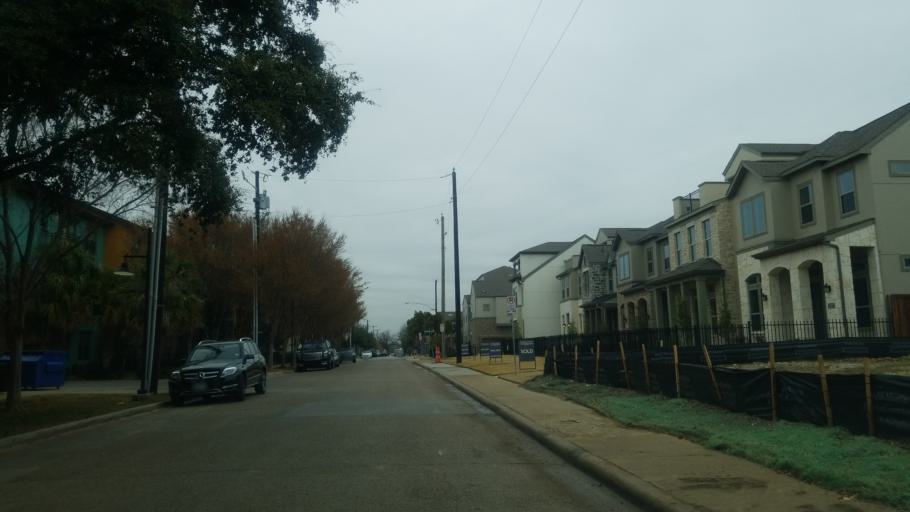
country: US
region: Texas
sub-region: Dallas County
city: Highland Park
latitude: 32.8260
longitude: -96.8182
